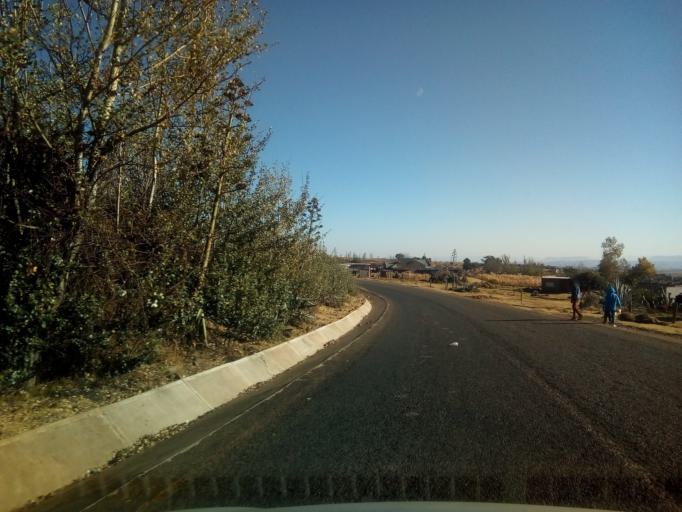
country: LS
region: Berea
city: Teyateyaneng
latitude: -29.2533
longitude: 27.7973
